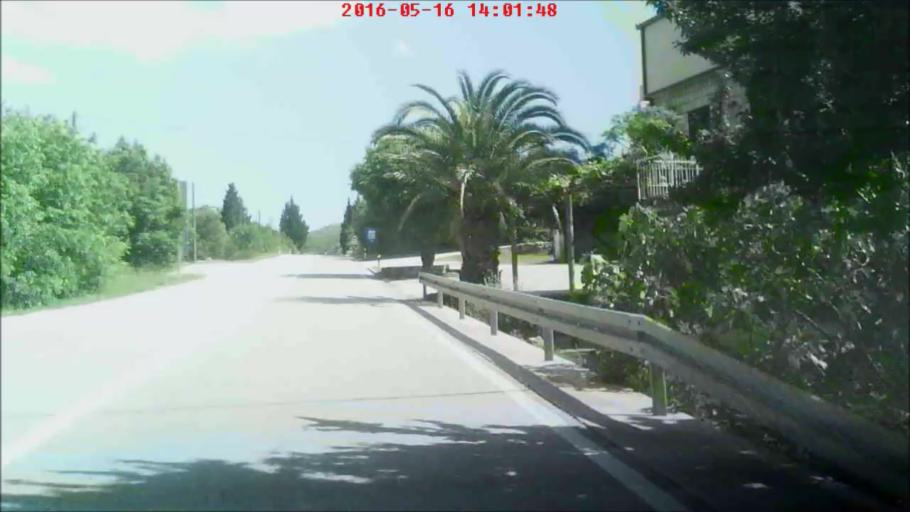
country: HR
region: Dubrovacko-Neretvanska
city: Ston
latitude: 42.8304
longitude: 17.7522
